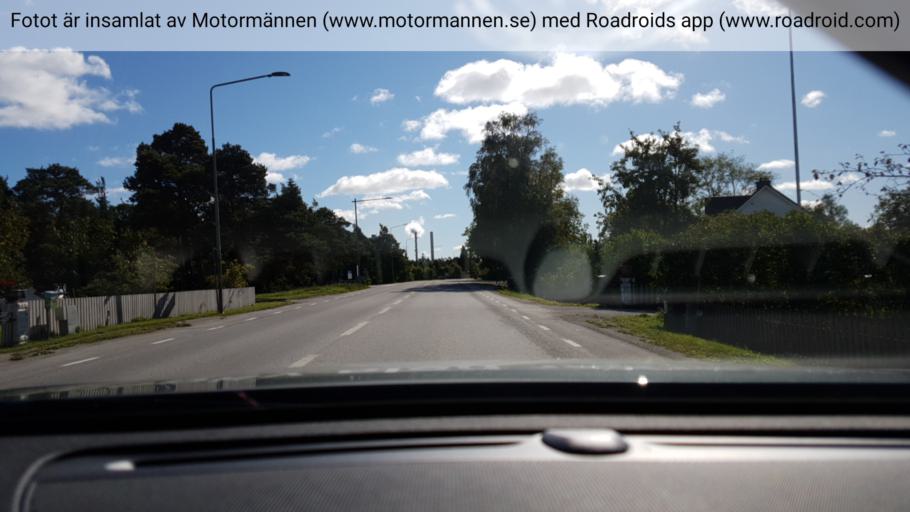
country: SE
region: Gotland
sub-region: Gotland
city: Slite
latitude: 57.7221
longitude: 18.7892
